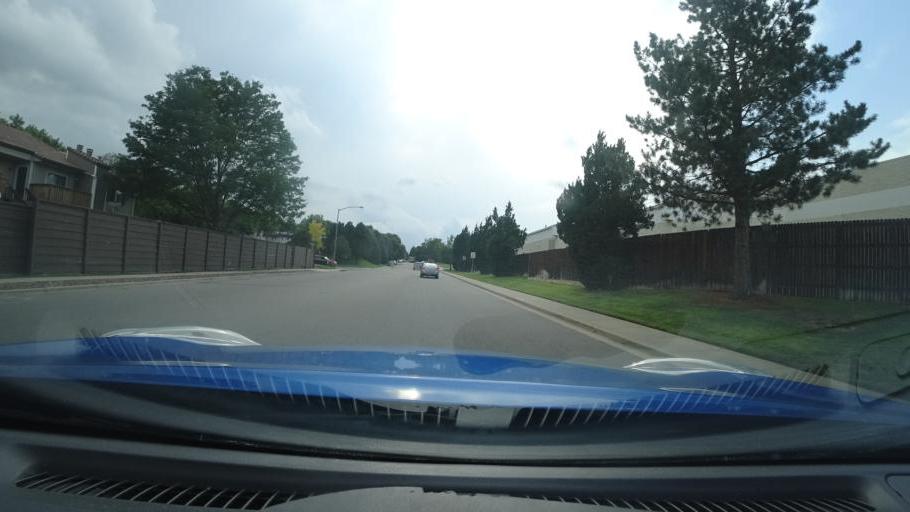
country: US
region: Colorado
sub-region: Adams County
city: Aurora
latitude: 39.6947
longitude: -104.8103
